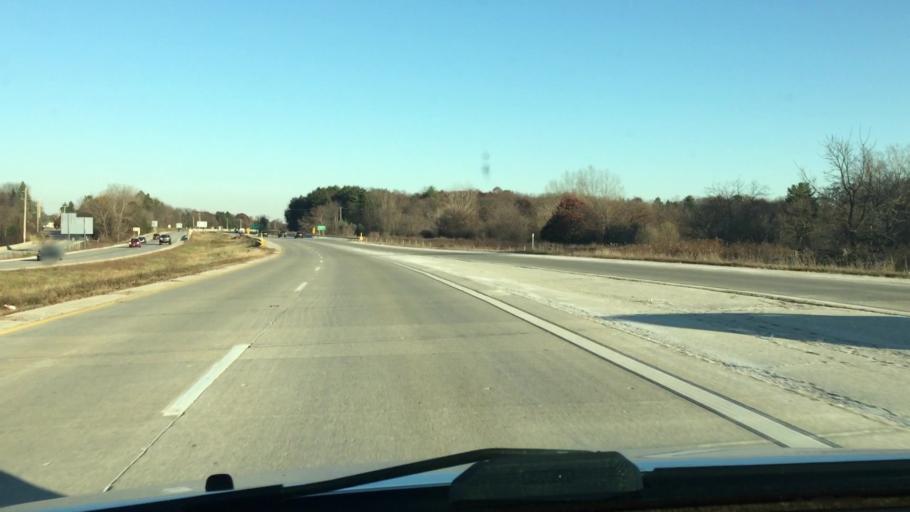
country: US
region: Wisconsin
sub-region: Waukesha County
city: Okauchee Lake
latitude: 43.1077
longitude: -88.4567
